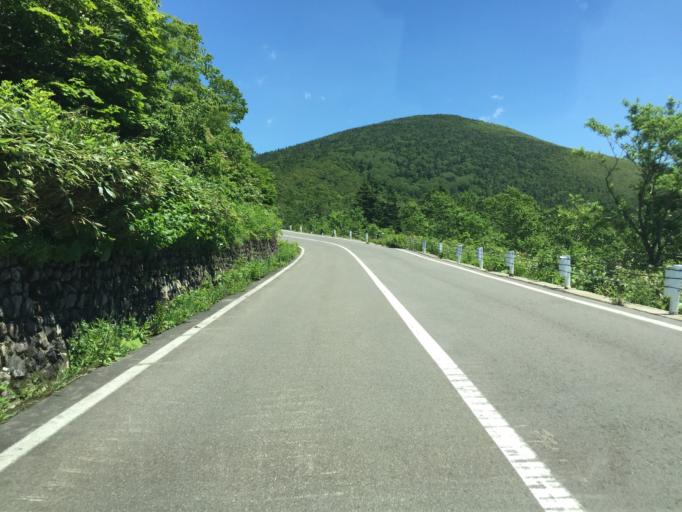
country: JP
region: Fukushima
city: Inawashiro
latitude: 37.6931
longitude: 140.2466
